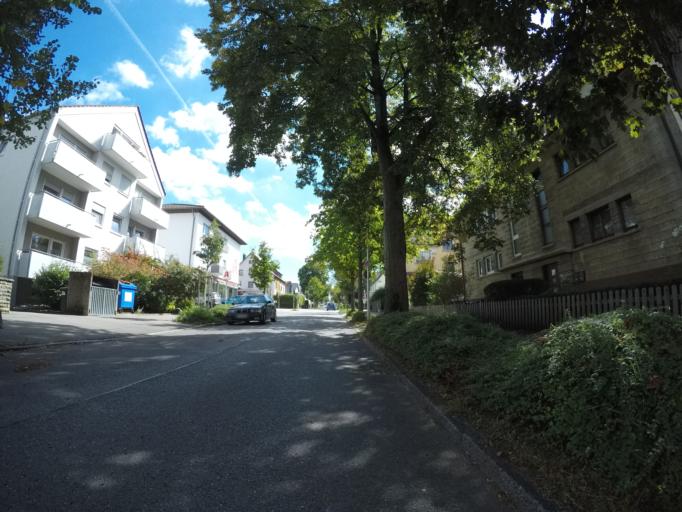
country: DE
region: Baden-Wuerttemberg
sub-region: Tuebingen Region
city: Reutlingen
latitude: 48.4827
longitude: 9.2063
